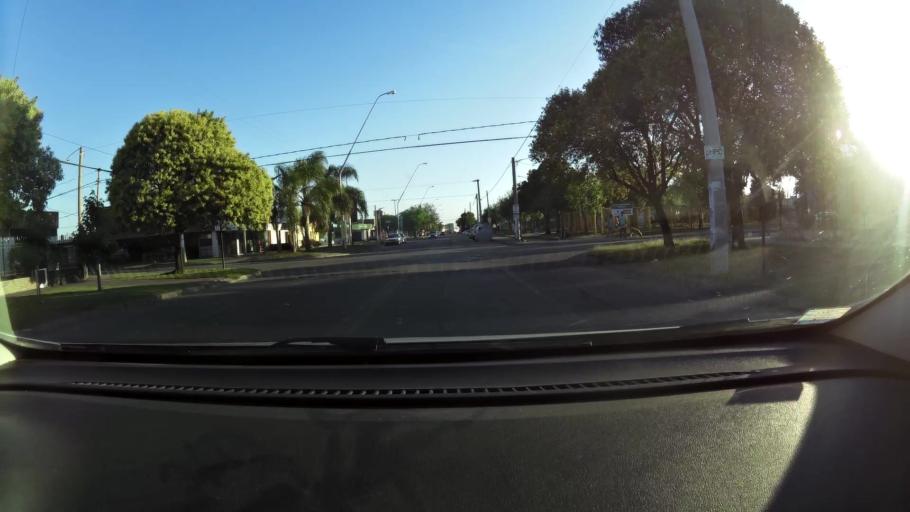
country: AR
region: Cordoba
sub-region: Departamento de Capital
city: Cordoba
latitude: -31.3766
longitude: -64.2143
